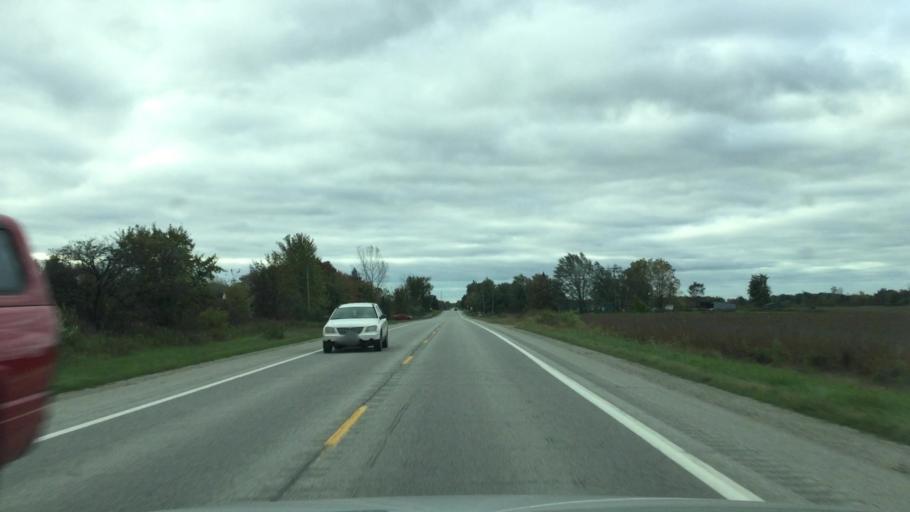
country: US
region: Michigan
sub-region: Macomb County
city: Memphis
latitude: 42.9466
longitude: -82.7626
